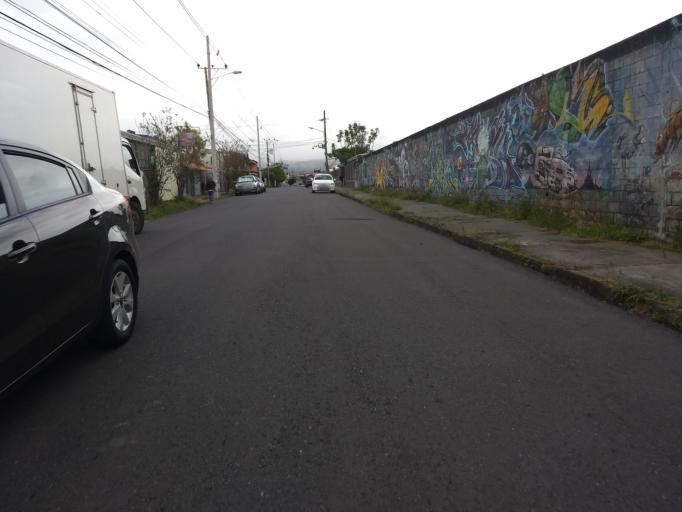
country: CR
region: San Jose
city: San Juan
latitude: 9.9566
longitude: -84.0811
